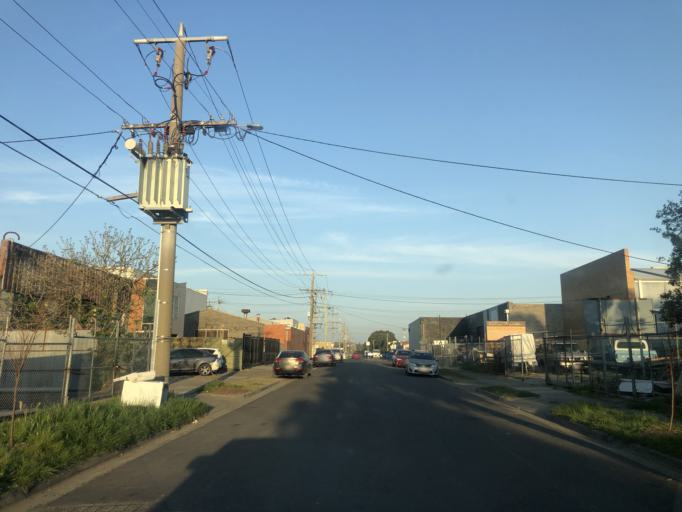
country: AU
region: Victoria
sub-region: Casey
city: Doveton
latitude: -37.9981
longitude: 145.2265
